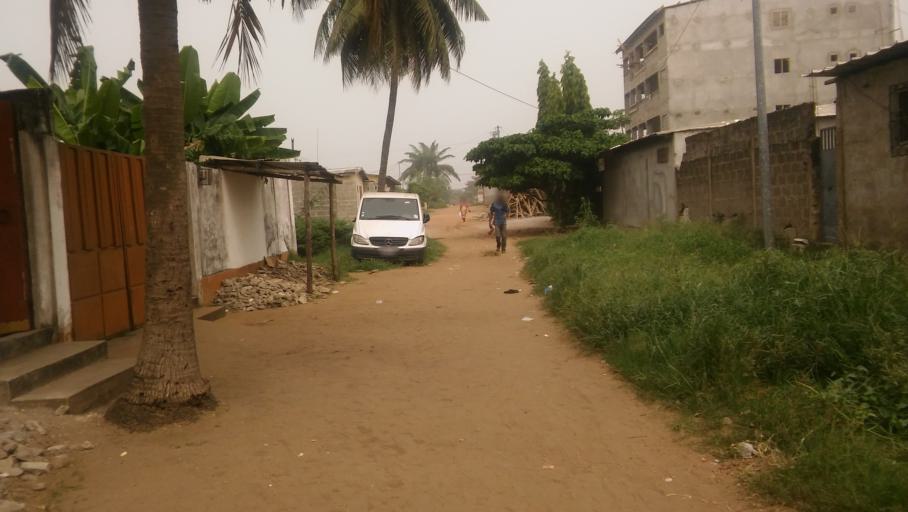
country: CI
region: Sud-Comoe
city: Grand-Bassam
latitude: 5.2178
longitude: -3.7312
